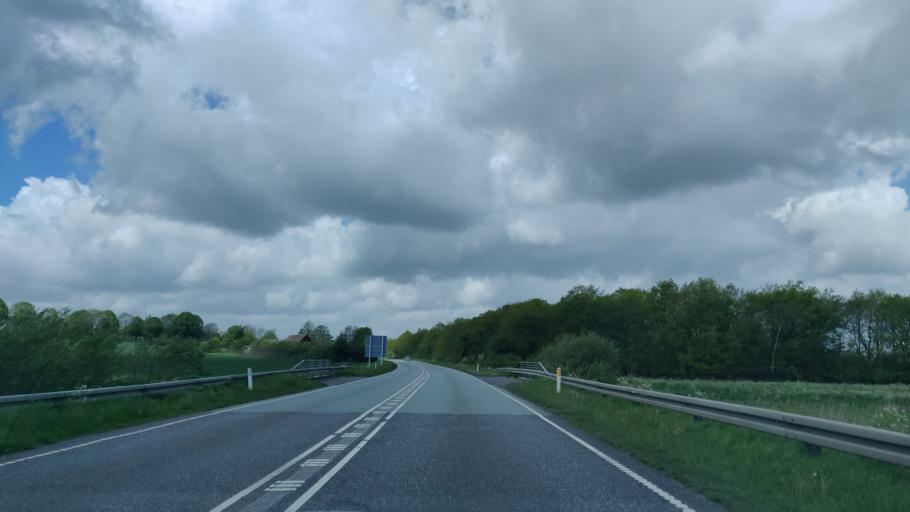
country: DK
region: Central Jutland
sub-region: Hedensted Kommune
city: Torring
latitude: 55.8395
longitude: 9.5064
